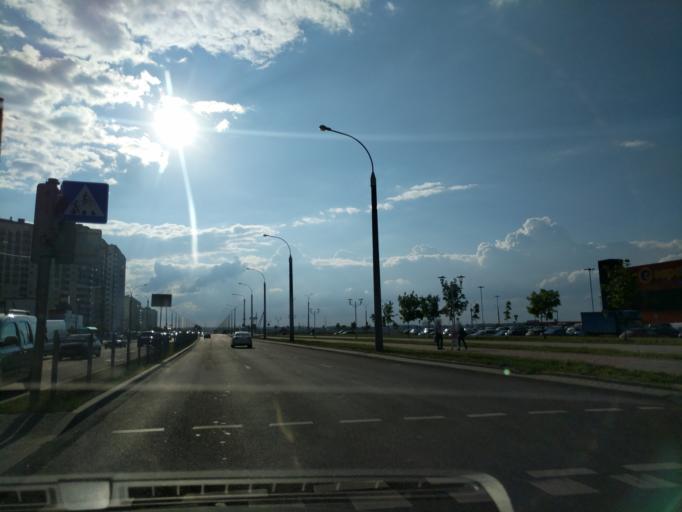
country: BY
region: Minsk
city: Zhdanovichy
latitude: 53.9164
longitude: 27.4302
